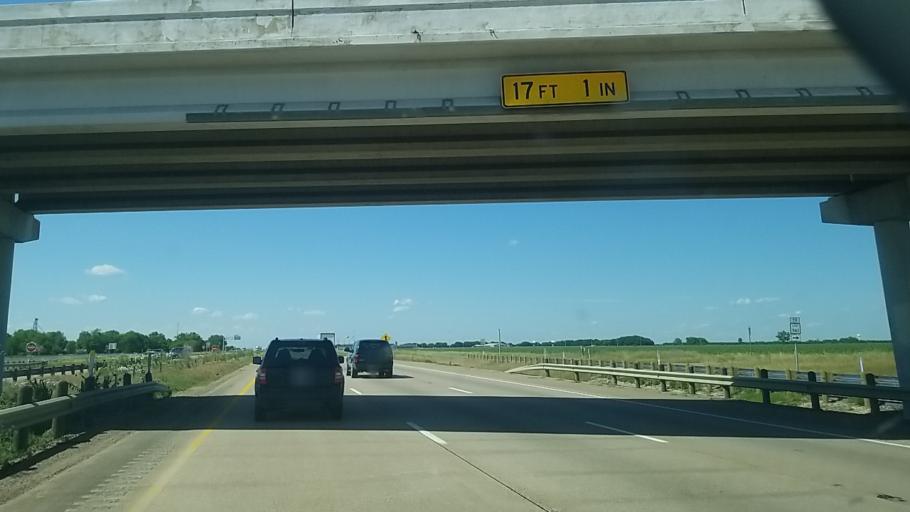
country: US
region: Texas
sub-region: Ellis County
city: Ferris
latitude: 32.4852
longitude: -96.6642
